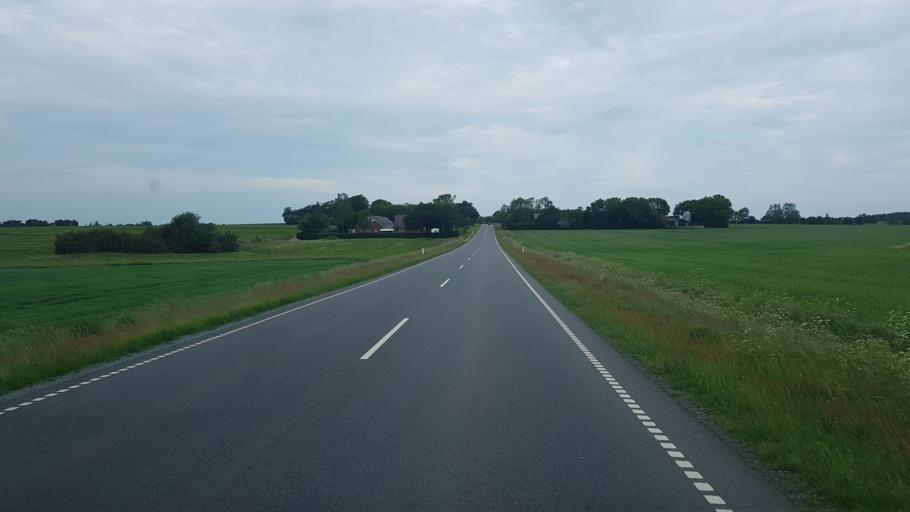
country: DK
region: South Denmark
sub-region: Vejen Kommune
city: Rodding
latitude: 55.4145
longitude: 9.0275
